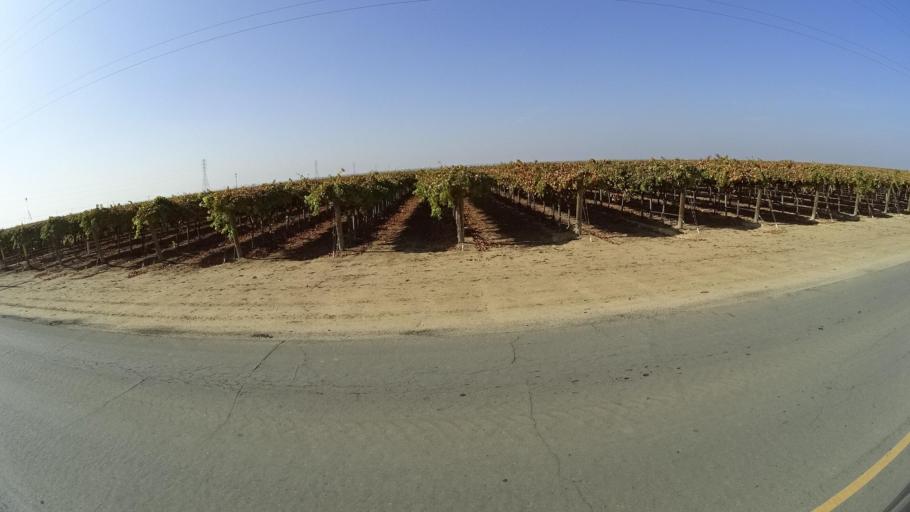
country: US
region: California
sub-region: Kern County
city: Greenacres
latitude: 35.5033
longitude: -119.1168
